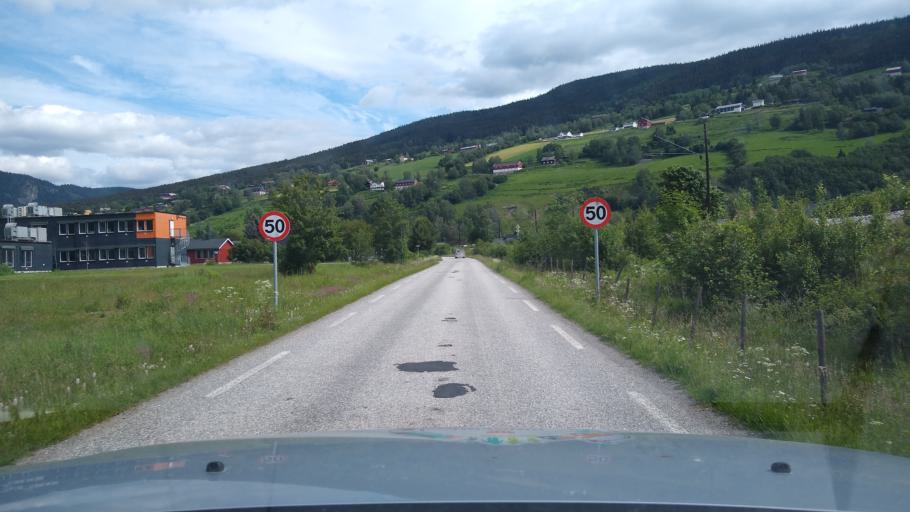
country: NO
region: Oppland
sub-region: Ringebu
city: Ringebu
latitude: 61.5233
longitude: 10.1472
